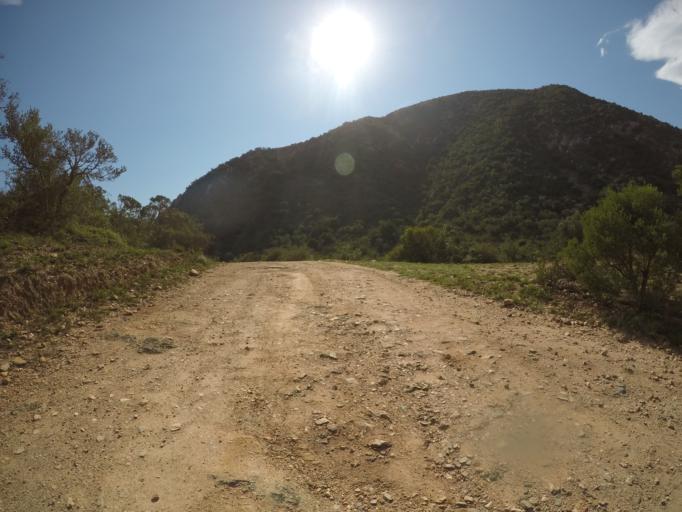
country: ZA
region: Eastern Cape
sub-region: Cacadu District Municipality
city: Kareedouw
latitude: -33.6571
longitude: 24.4311
